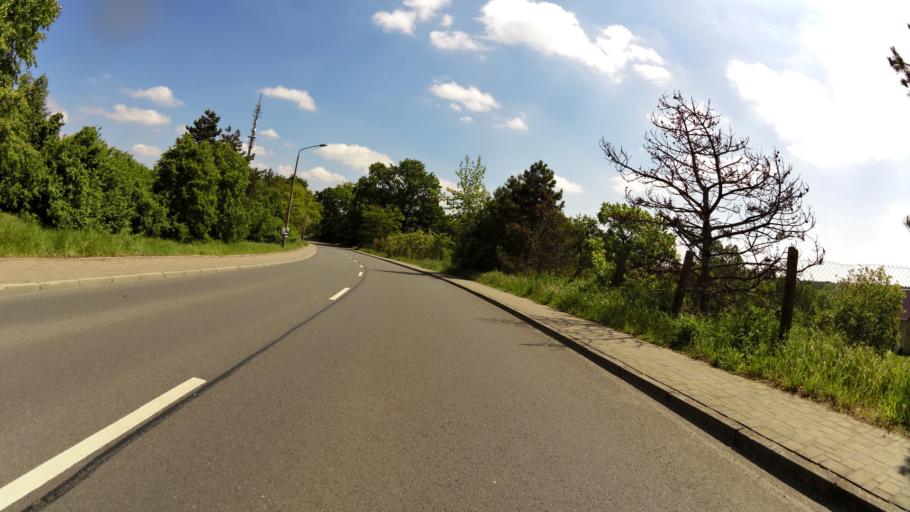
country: DE
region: Saxony
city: Belgern
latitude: 51.4784
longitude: 13.1231
